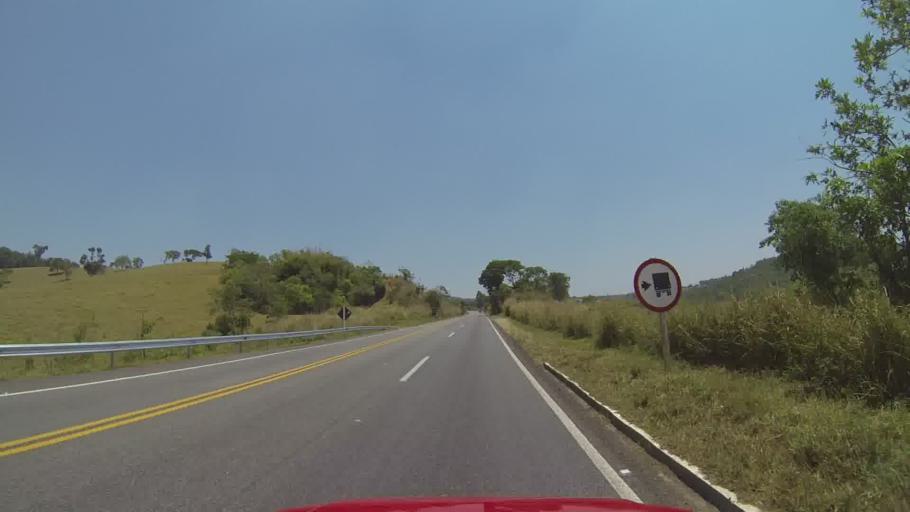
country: BR
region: Minas Gerais
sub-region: Itapecerica
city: Itapecerica
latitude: -20.2602
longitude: -45.0959
